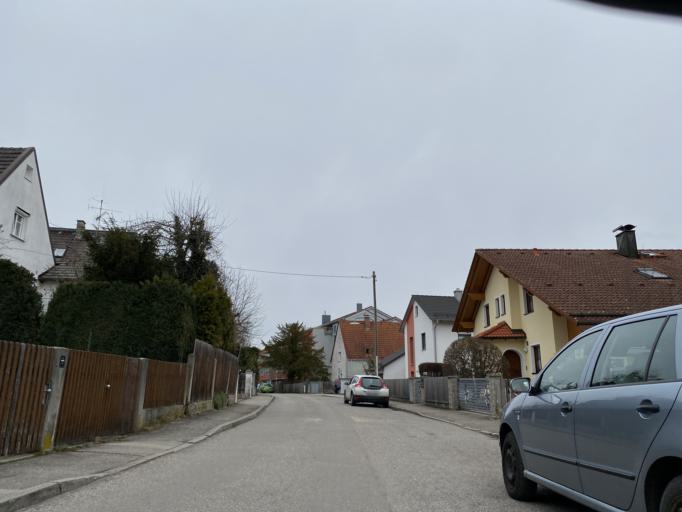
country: DE
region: Bavaria
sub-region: Upper Bavaria
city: Fuerstenfeldbruck
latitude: 48.1790
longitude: 11.2434
